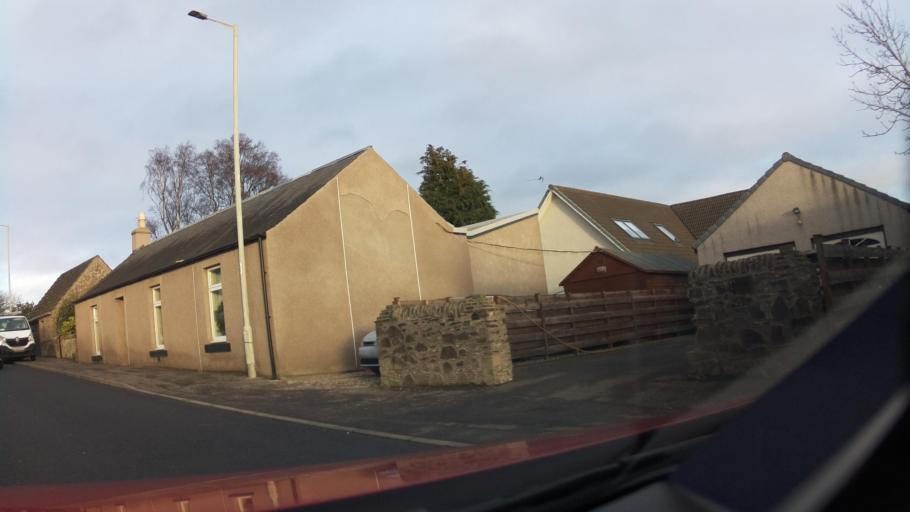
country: GB
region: Scotland
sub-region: Fife
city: Tayport
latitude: 56.5134
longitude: -2.8173
